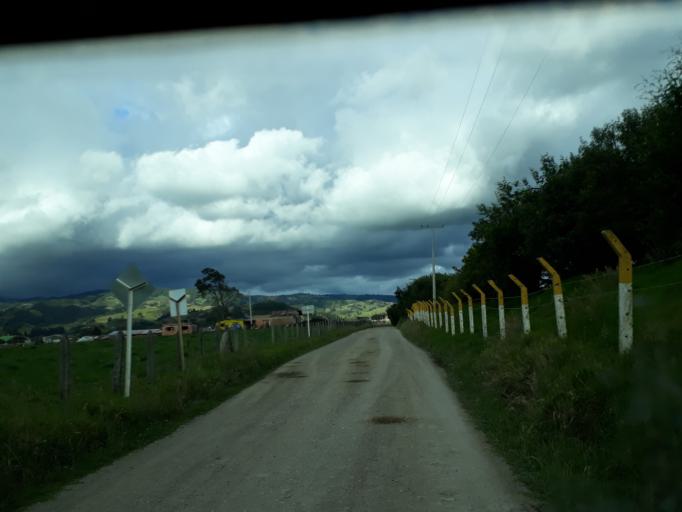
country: CO
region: Cundinamarca
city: Carmen de Carupa
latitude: 5.3519
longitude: -73.9114
